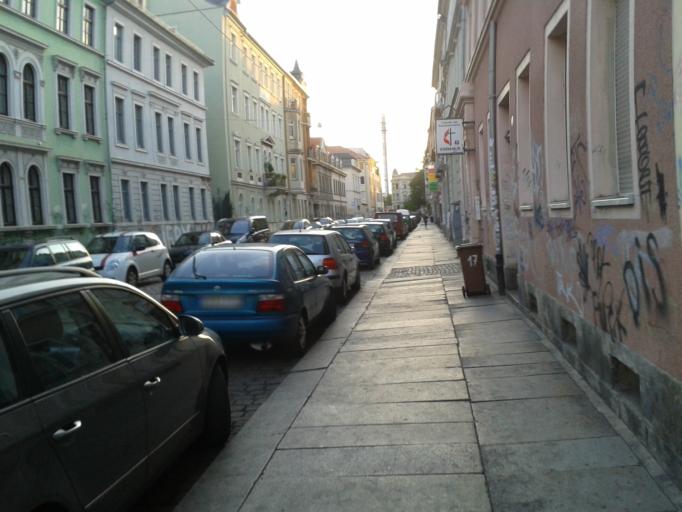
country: DE
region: Saxony
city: Dresden
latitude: 51.0663
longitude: 13.7503
